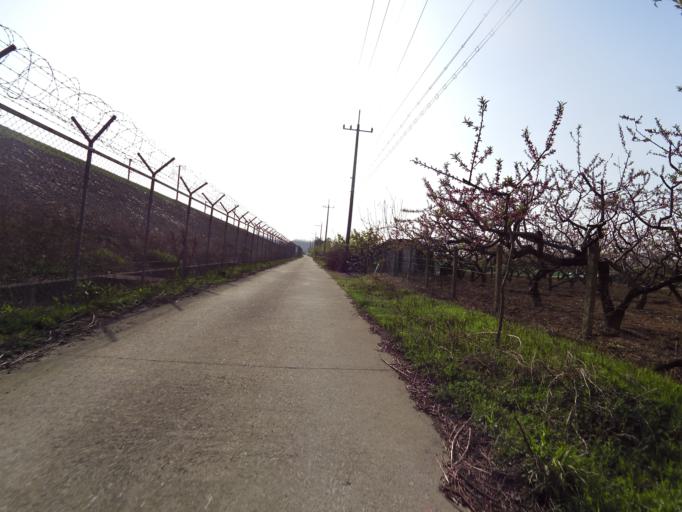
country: KR
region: Gyeongsangbuk-do
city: Gyeongsan-si
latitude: 35.8551
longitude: 128.7002
